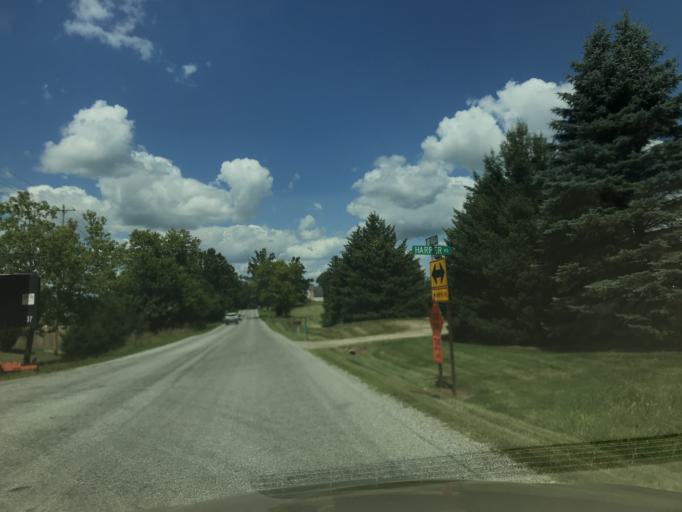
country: US
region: Michigan
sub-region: Ingham County
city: Holt
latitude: 42.6113
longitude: -84.5625
